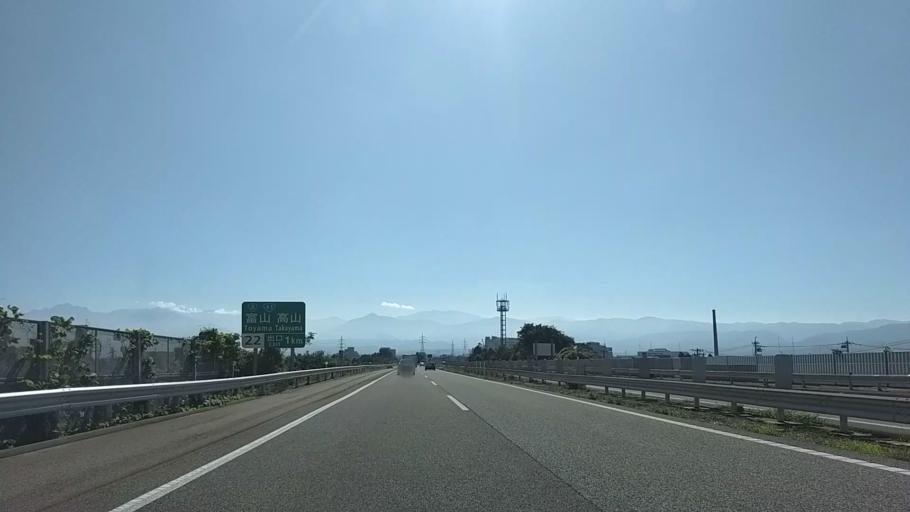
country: JP
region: Toyama
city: Toyama-shi
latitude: 36.6616
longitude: 137.1954
